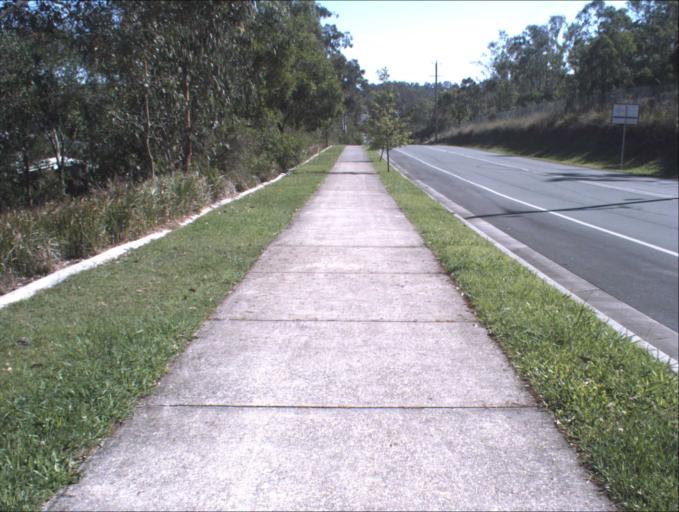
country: AU
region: Queensland
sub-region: Logan
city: Windaroo
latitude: -27.7228
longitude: 153.1737
